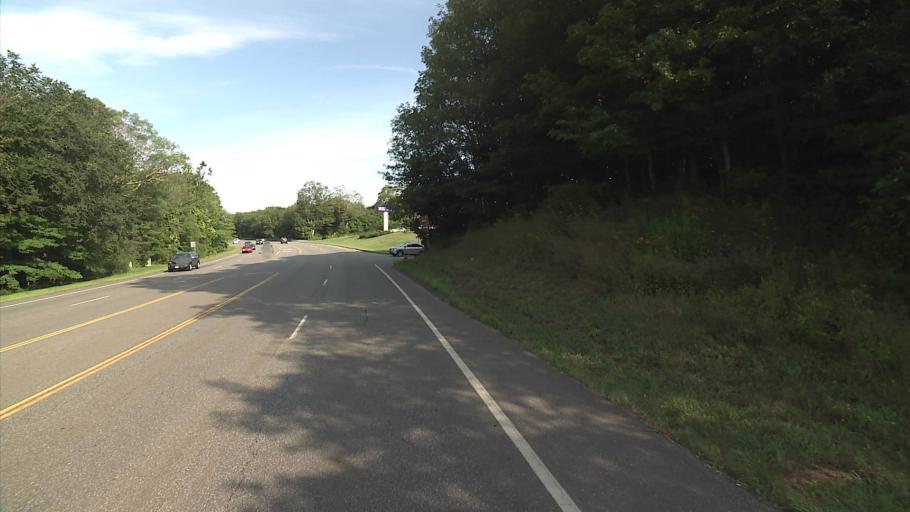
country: US
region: Connecticut
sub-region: New London County
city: Preston City
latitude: 41.4869
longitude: -71.9715
